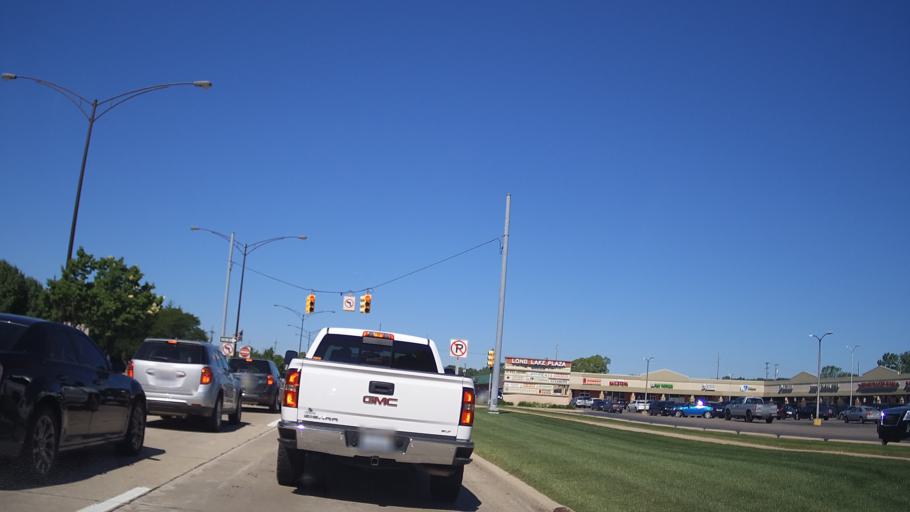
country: US
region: Michigan
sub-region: Oakland County
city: Troy
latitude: 42.5923
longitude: -83.1256
